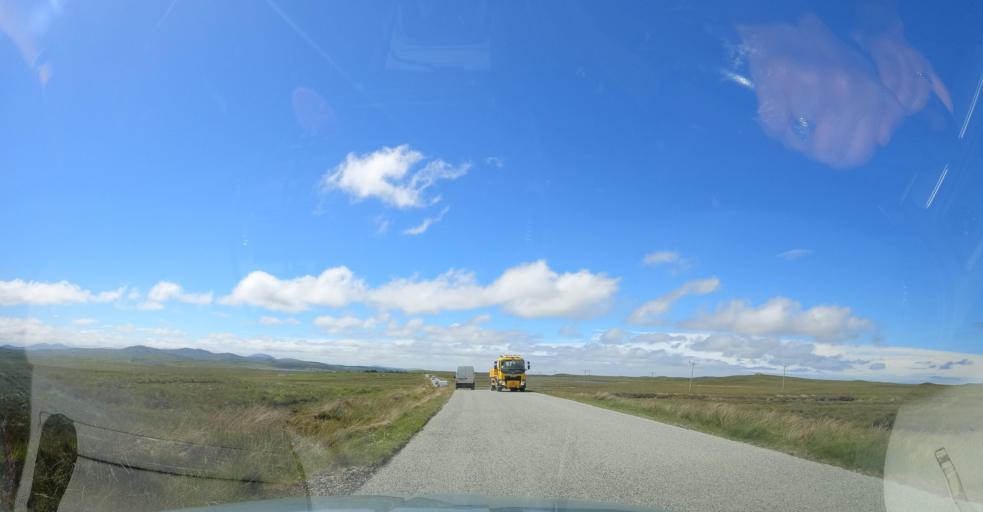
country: GB
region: Scotland
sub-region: Eilean Siar
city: Isle of Lewis
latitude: 58.1854
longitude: -6.6778
